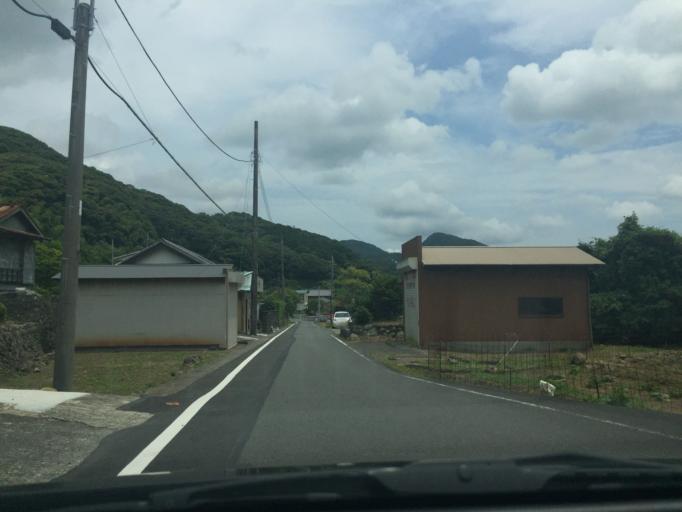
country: JP
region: Shizuoka
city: Shimoda
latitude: 34.6854
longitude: 138.8122
